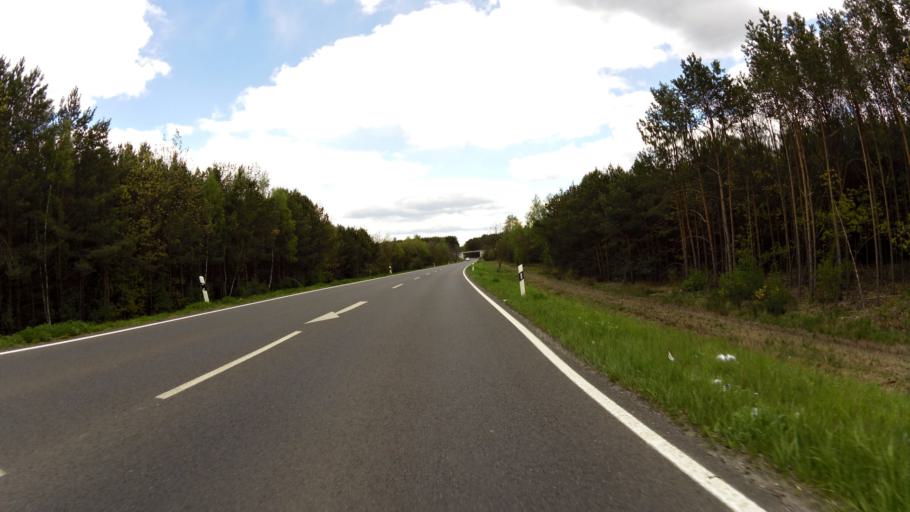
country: DE
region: Brandenburg
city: Langewahl
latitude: 52.3221
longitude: 14.1152
